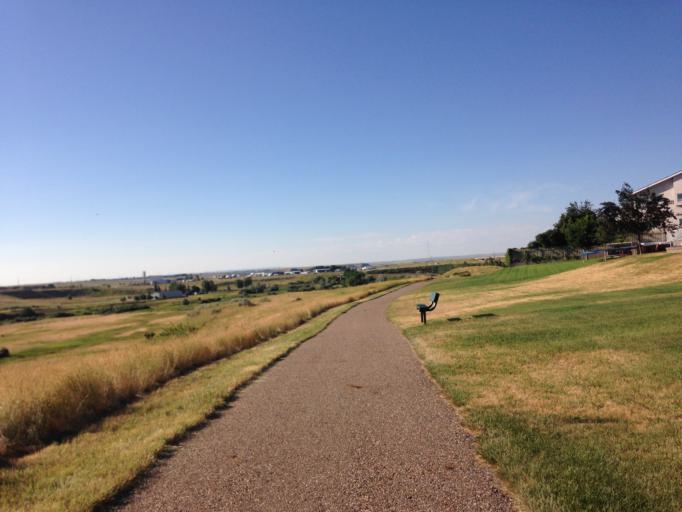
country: CA
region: Alberta
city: Medicine Hat
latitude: 49.9953
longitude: -110.6223
